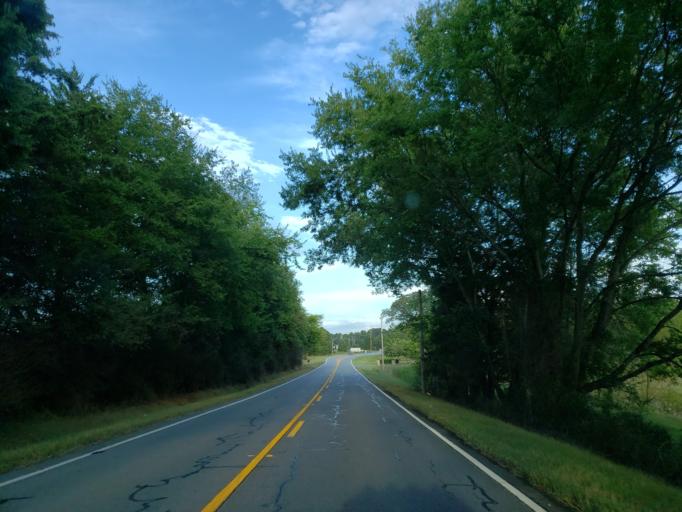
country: US
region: Georgia
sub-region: Bartow County
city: Euharlee
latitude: 34.2410
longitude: -84.8835
